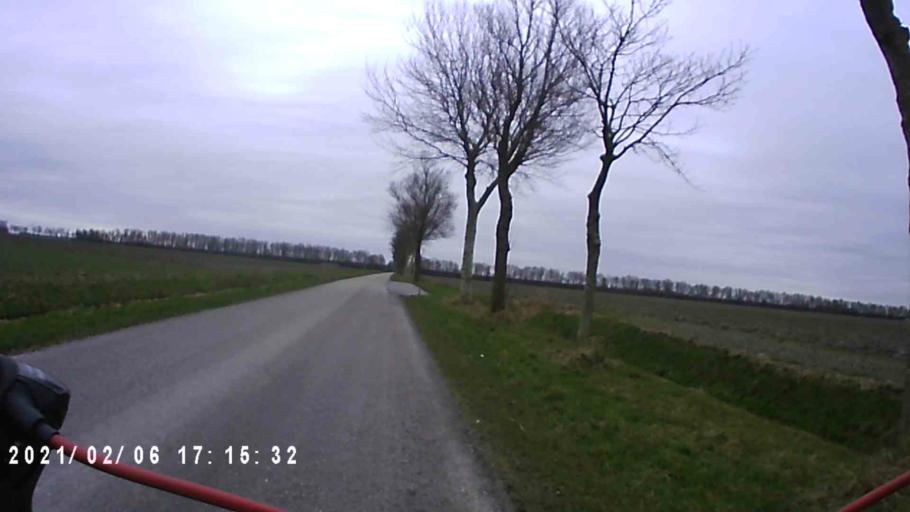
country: NL
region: Groningen
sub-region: Gemeente Appingedam
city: Appingedam
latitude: 53.4237
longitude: 6.7793
